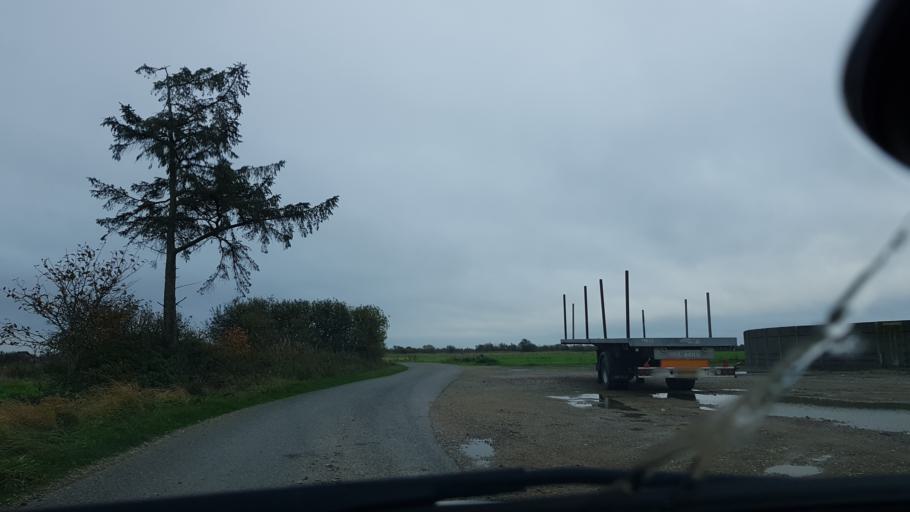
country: DK
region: South Denmark
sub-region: Esbjerg Kommune
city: Ribe
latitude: 55.2562
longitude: 8.8292
